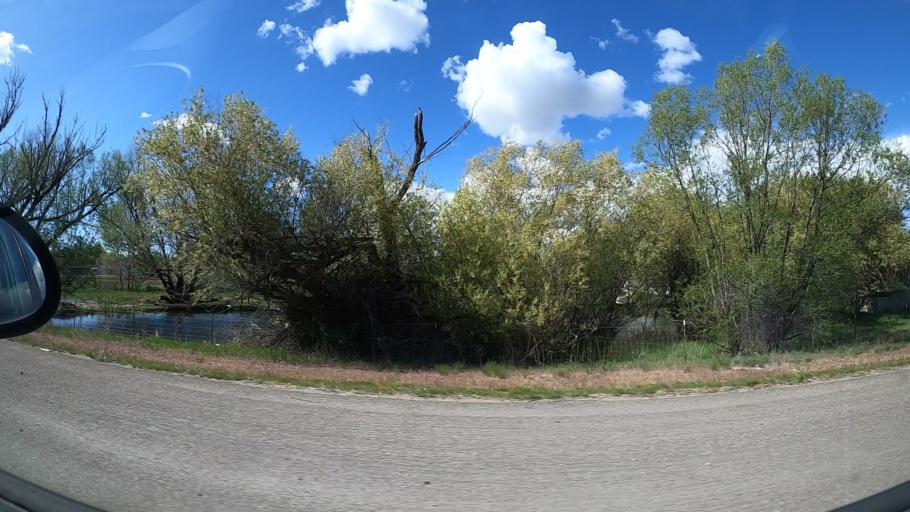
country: US
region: Idaho
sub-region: Ada County
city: Eagle
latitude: 43.6922
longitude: -116.3650
